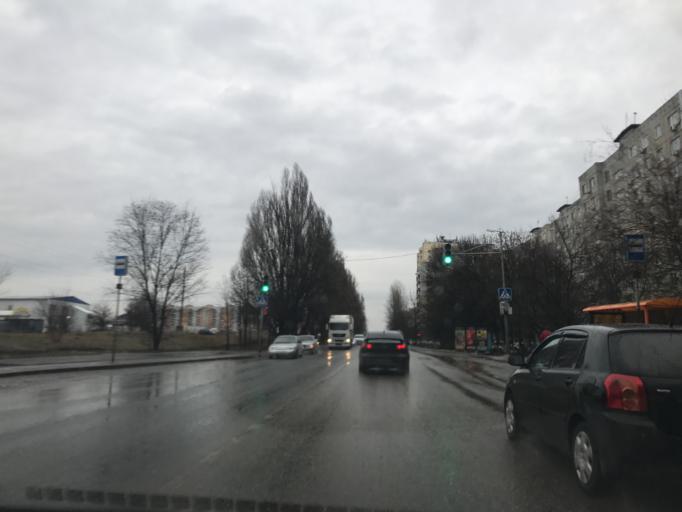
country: RU
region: Rostov
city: Severnyy
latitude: 47.3005
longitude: 39.7145
